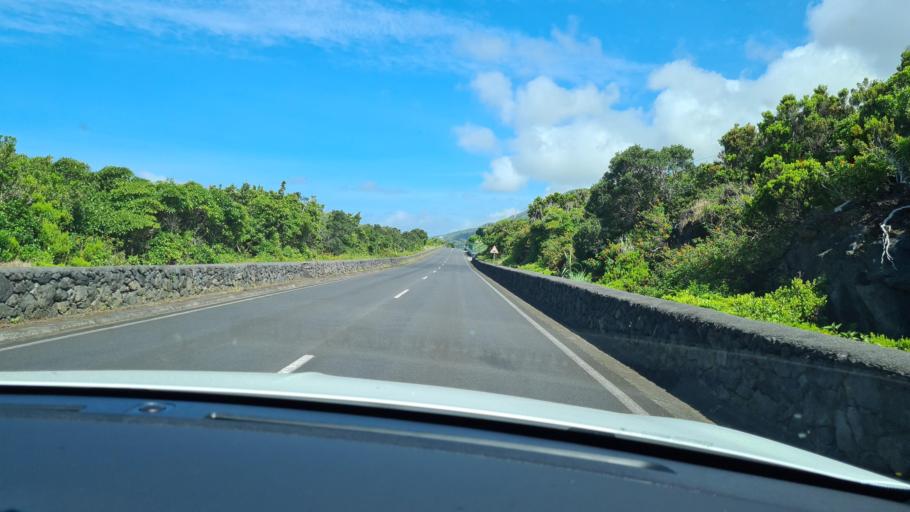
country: PT
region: Azores
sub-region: Sao Roque do Pico
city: Sao Roque do Pico
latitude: 38.6530
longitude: -28.1495
